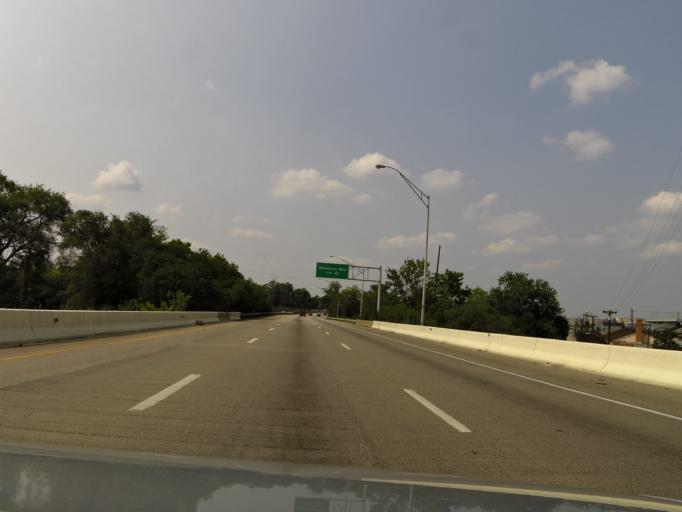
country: US
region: Ohio
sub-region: Hamilton County
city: Reading
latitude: 39.2276
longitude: -84.4494
